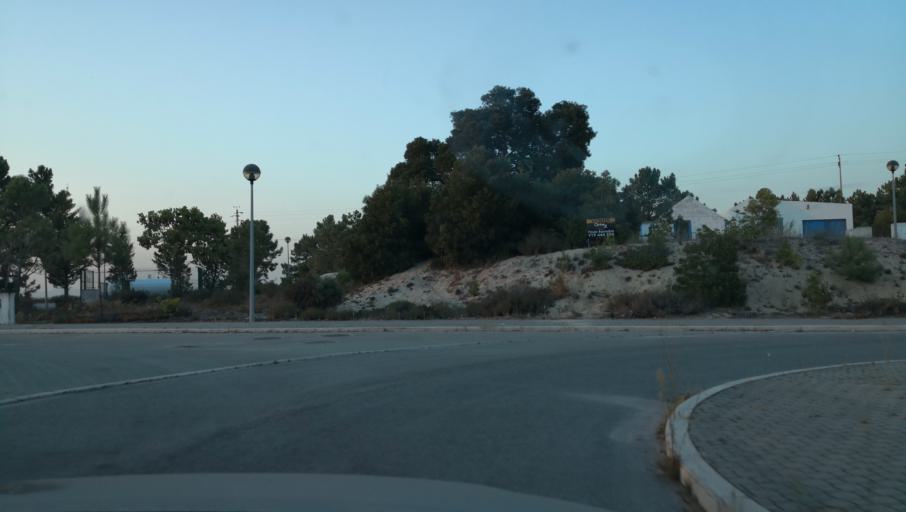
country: PT
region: Setubal
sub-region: Setubal
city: Setubal
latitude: 38.3988
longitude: -8.7728
